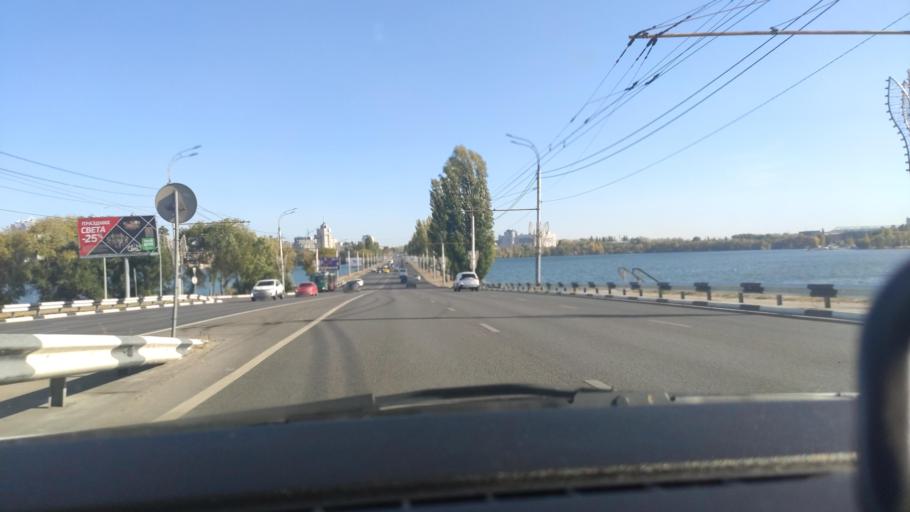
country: RU
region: Voronezj
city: Voronezh
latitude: 51.6672
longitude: 39.2275
